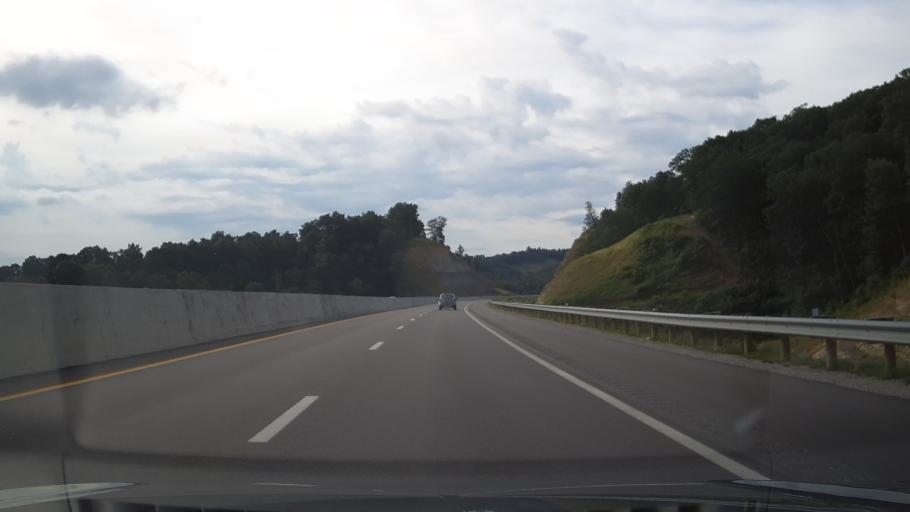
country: US
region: Ohio
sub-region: Scioto County
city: Lucasville
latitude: 38.8762
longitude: -82.9438
